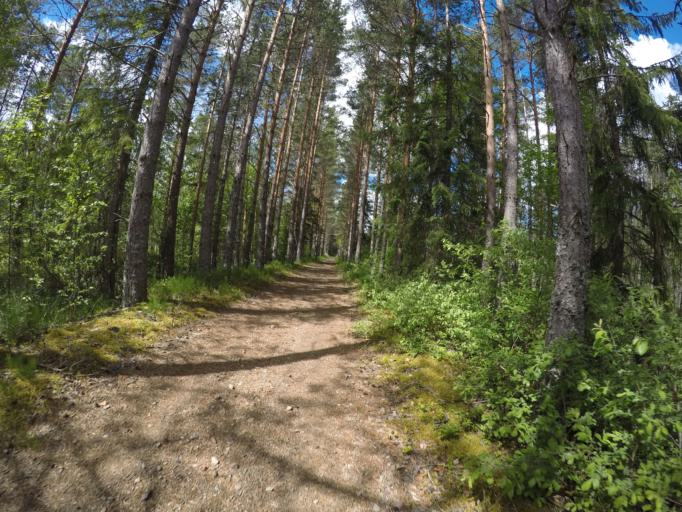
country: SE
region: Vaermland
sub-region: Filipstads Kommun
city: Lesjofors
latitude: 60.1393
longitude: 14.2908
